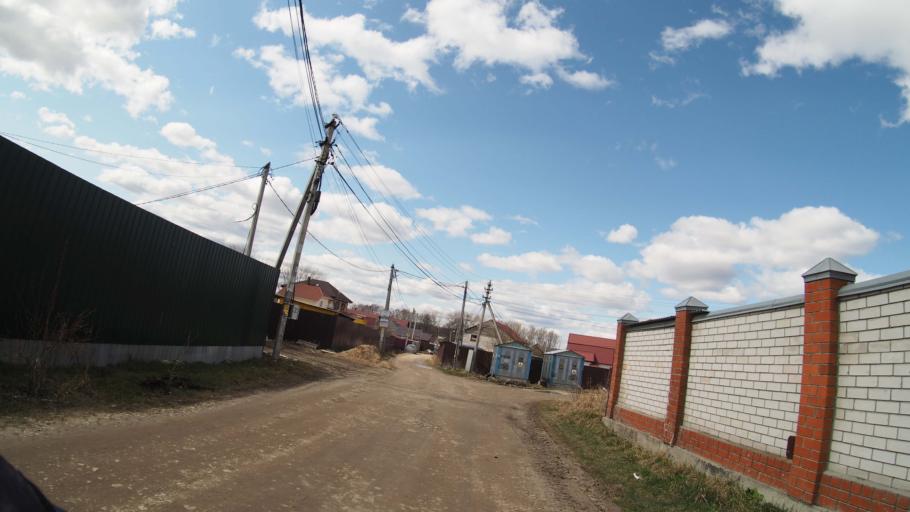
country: RU
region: Moskovskaya
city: Malyshevo
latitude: 55.5332
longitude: 38.3156
